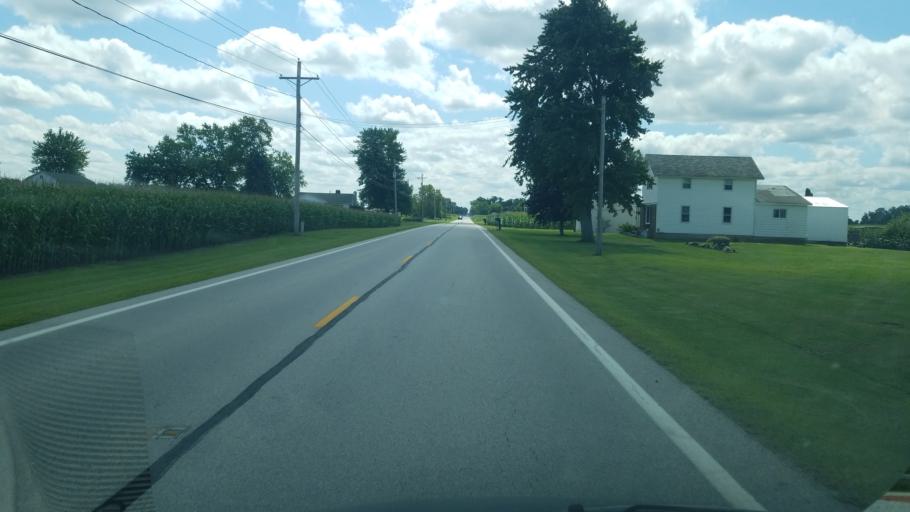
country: US
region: Ohio
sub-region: Henry County
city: Liberty Center
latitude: 41.4935
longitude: -84.0088
